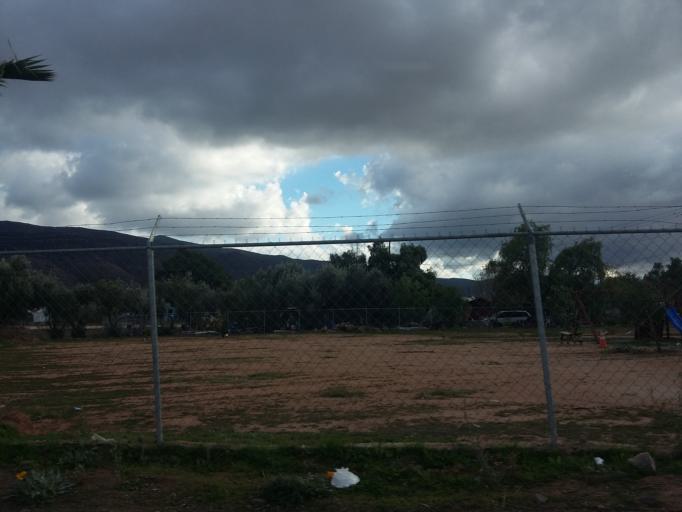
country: MX
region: Baja California
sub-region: Ensenada
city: Rancho Verde
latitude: 32.0915
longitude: -116.5818
